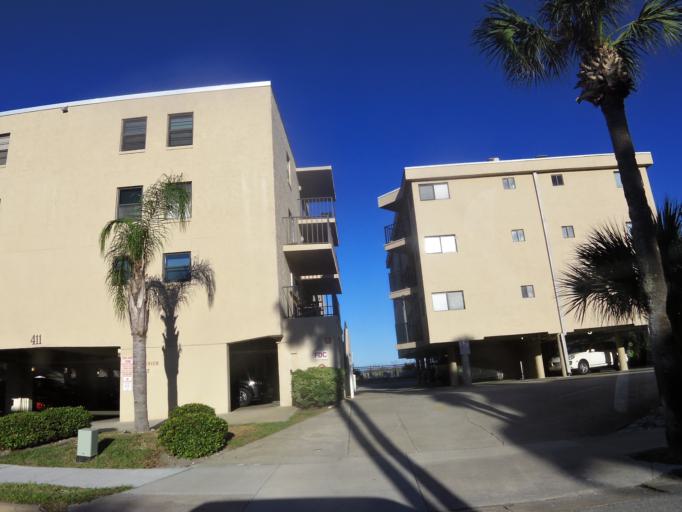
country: US
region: Florida
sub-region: Duval County
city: Jacksonville Beach
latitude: 30.2845
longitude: -81.3887
